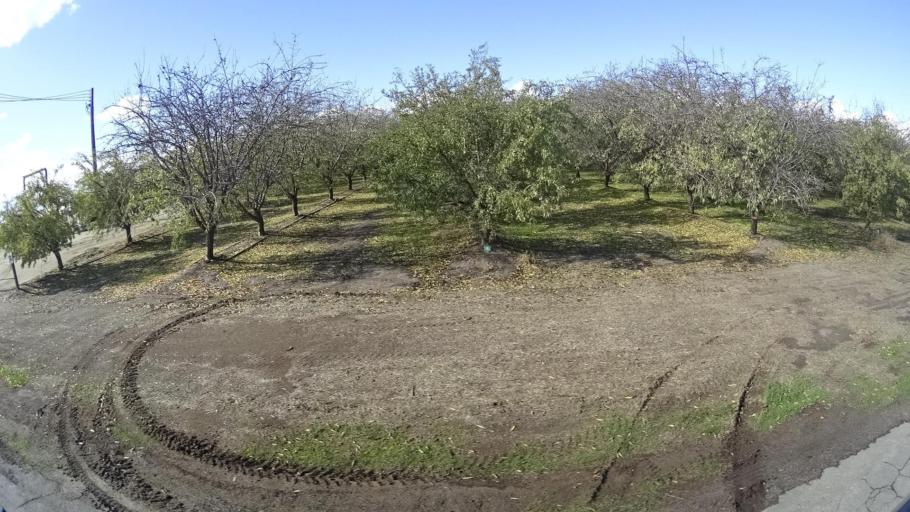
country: US
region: California
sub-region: Kern County
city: Greenacres
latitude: 35.2639
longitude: -119.1284
